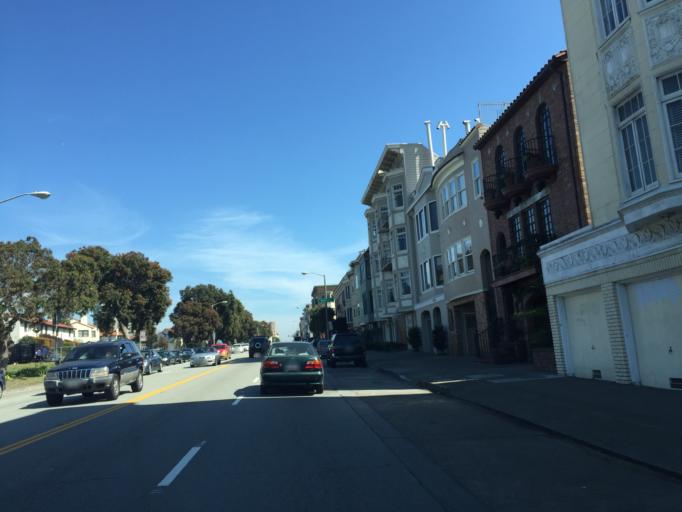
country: US
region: California
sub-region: San Francisco County
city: San Francisco
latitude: 37.8035
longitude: -122.4298
